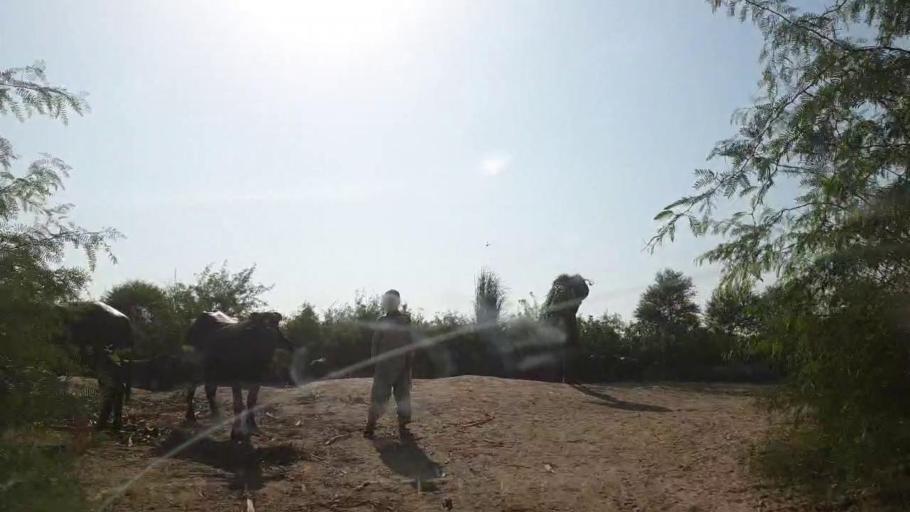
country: PK
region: Sindh
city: Tando Jam
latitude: 25.3480
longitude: 68.5732
